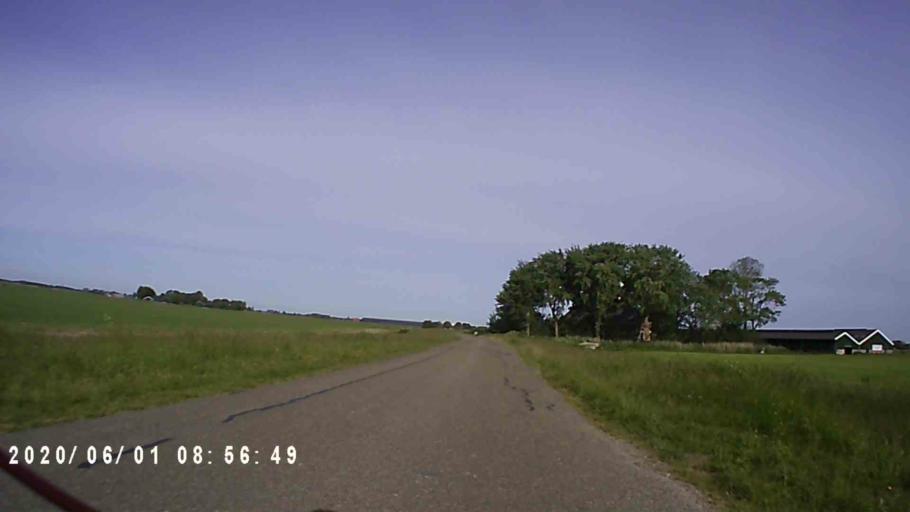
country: NL
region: Friesland
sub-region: Gemeente Leeuwarderadeel
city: Britsum
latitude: 53.2800
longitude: 5.8166
